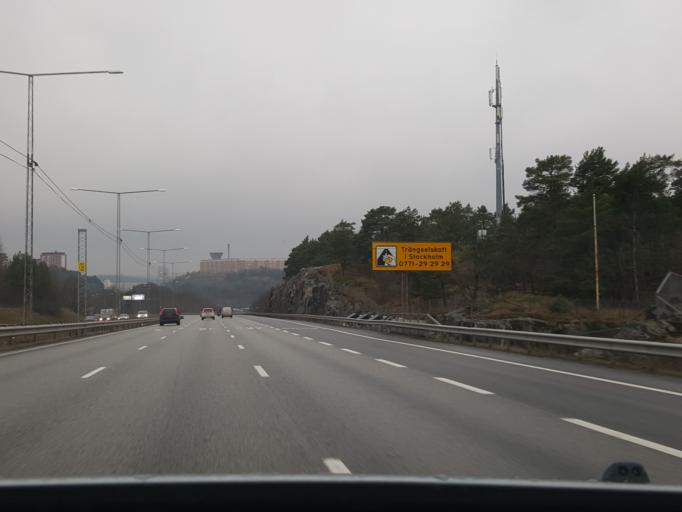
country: SE
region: Stockholm
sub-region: Nacka Kommun
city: Nacka
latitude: 59.3109
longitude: 18.1419
